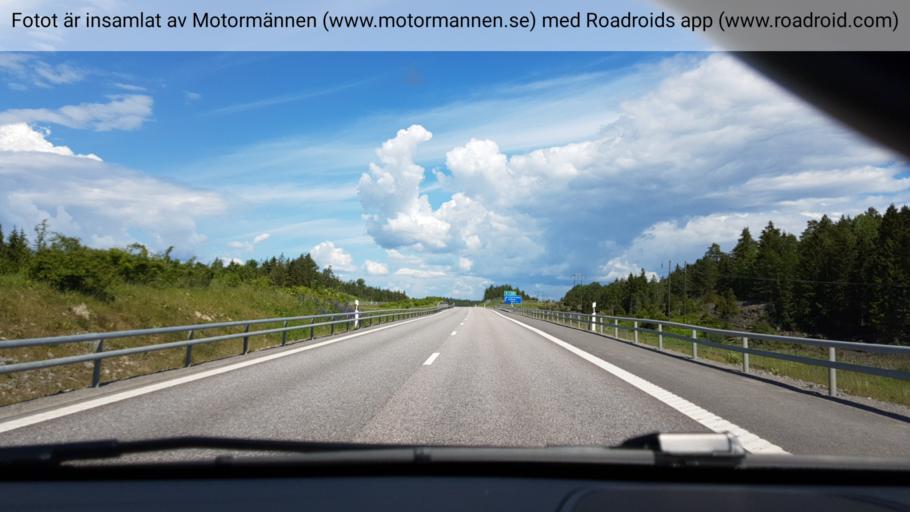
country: SE
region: Stockholm
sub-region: Nynashamns Kommun
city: Osmo
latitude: 59.0140
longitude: 17.9463
